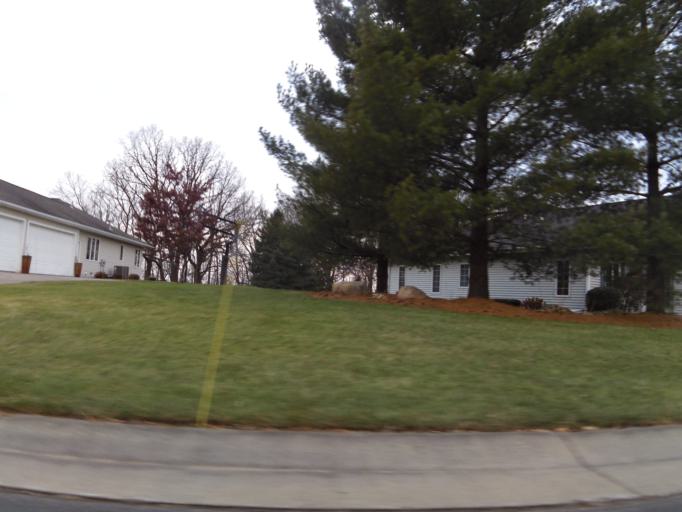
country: US
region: Wisconsin
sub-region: Pierce County
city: River Falls
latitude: 44.8613
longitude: -92.6032
